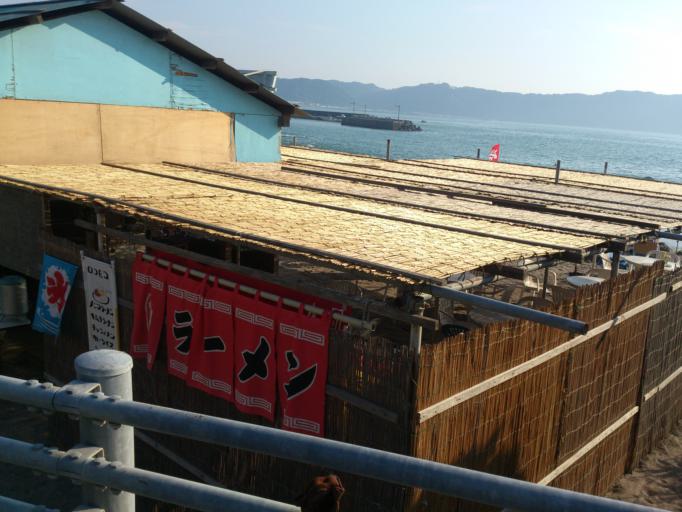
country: JP
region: Chiba
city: Tateyama
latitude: 35.0517
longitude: 139.8321
